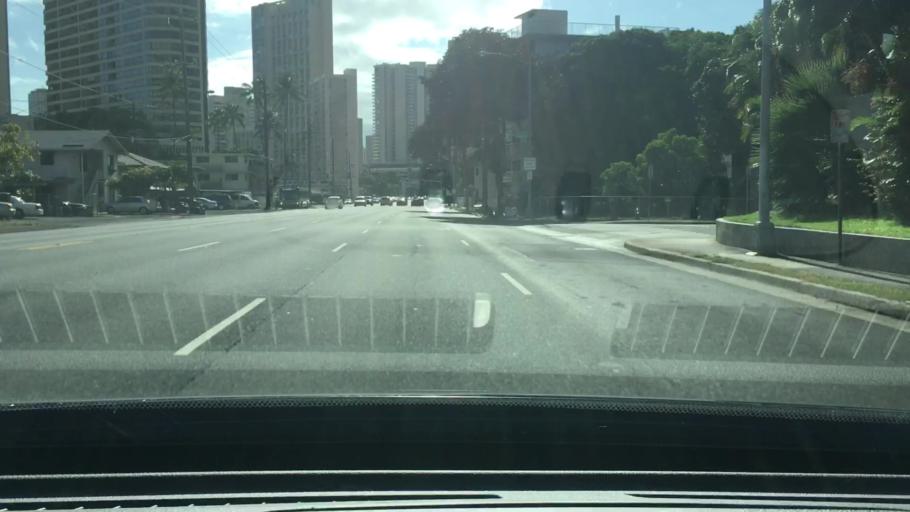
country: US
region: Hawaii
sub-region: Honolulu County
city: Honolulu
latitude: 21.2877
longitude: -157.8217
